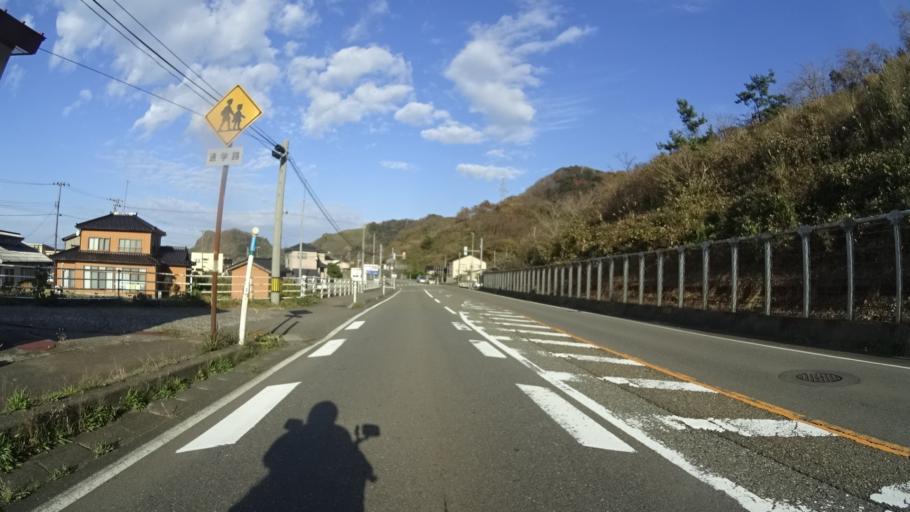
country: JP
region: Niigata
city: Kashiwazaki
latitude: 37.3159
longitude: 138.4326
